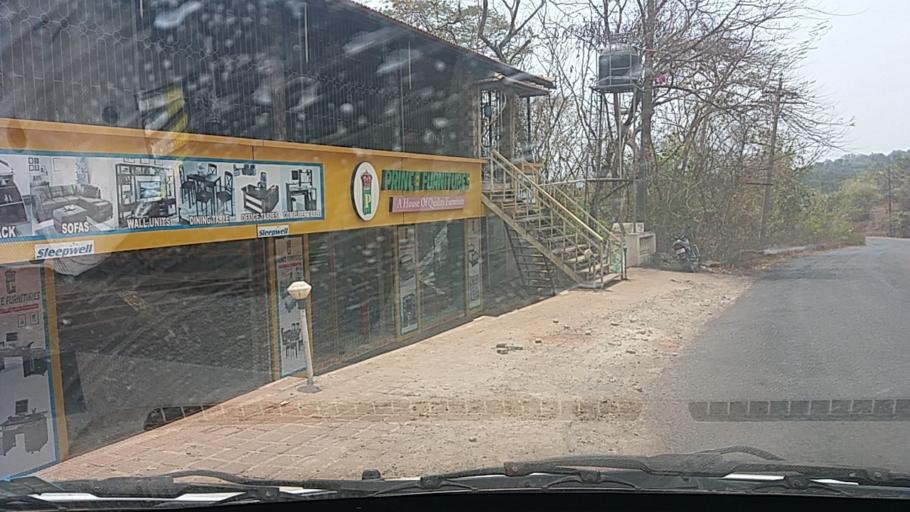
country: IN
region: Goa
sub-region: North Goa
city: Saligao
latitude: 15.5297
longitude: 73.7999
